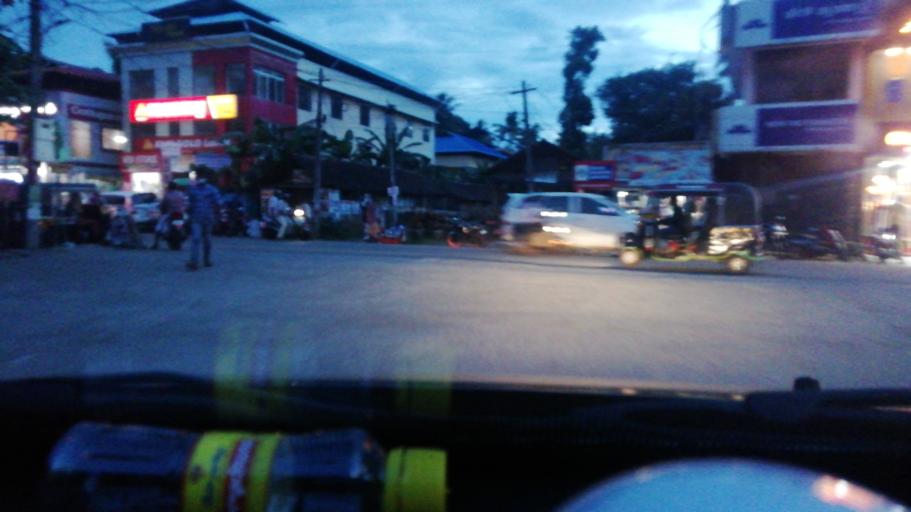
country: IN
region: Kerala
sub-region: Thiruvananthapuram
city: Paravur
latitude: 8.8108
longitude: 76.6688
